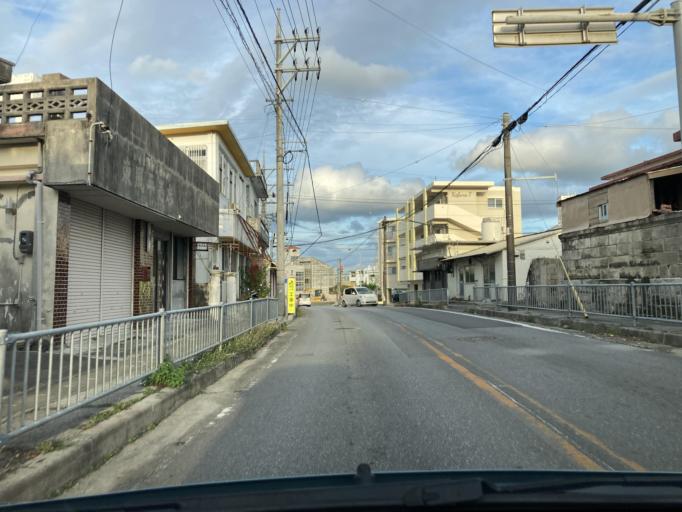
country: JP
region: Okinawa
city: Tomigusuku
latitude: 26.1527
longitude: 127.7200
